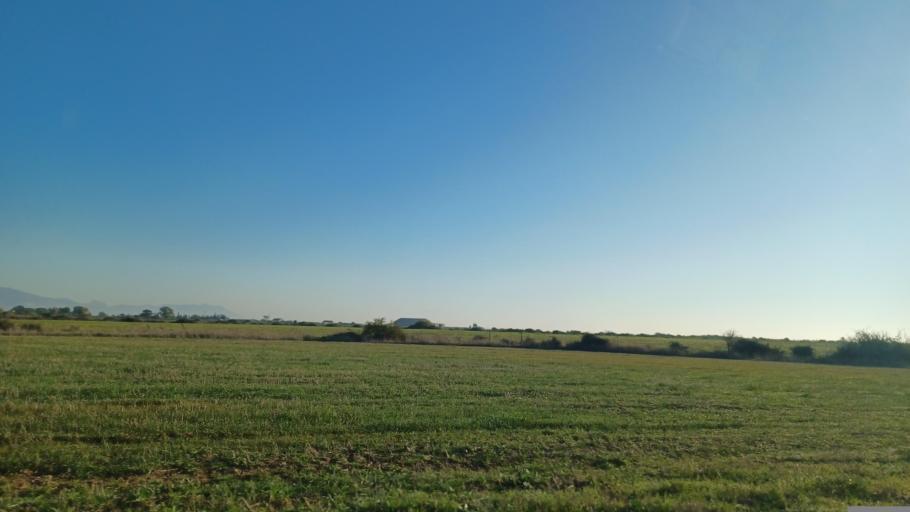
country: CY
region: Lefkosia
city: Kato Deftera
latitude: 35.1434
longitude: 33.2731
